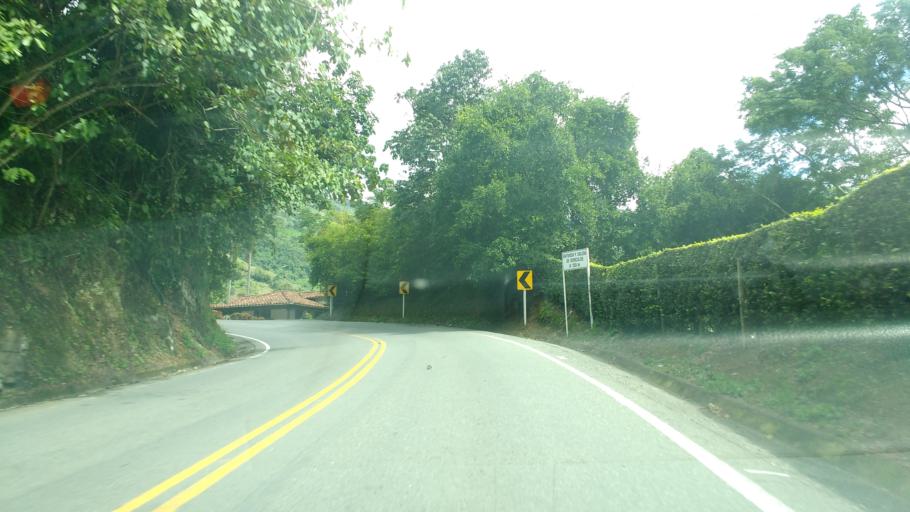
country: CO
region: Antioquia
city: Titiribi
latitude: 6.0410
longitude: -75.7601
